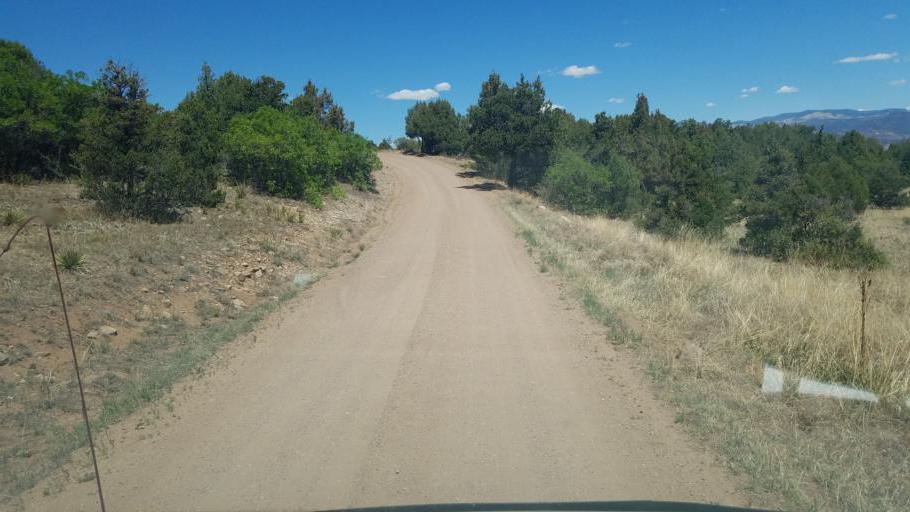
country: US
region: Colorado
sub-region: Custer County
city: Westcliffe
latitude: 38.3031
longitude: -105.6712
